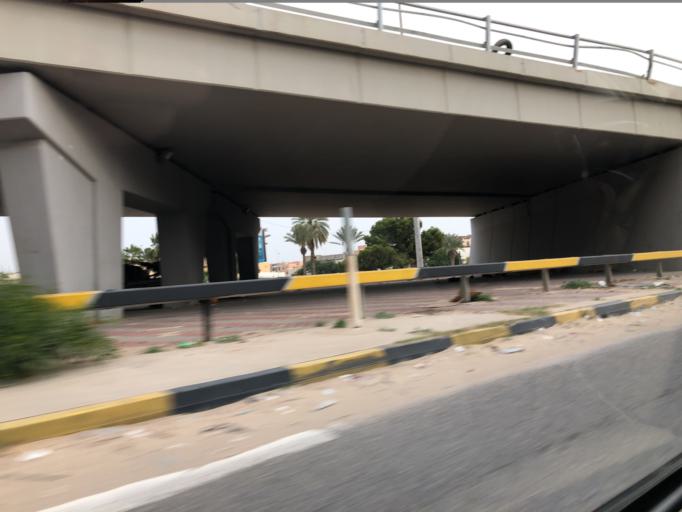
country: LY
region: Tripoli
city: Tripoli
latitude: 32.8675
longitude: 13.1384
